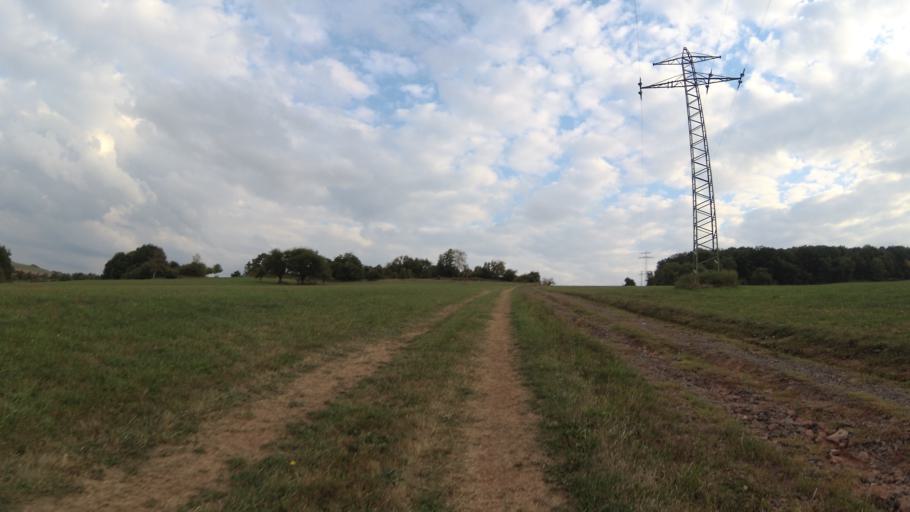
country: DE
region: Saarland
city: Ottweiler
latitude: 49.4252
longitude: 7.1504
